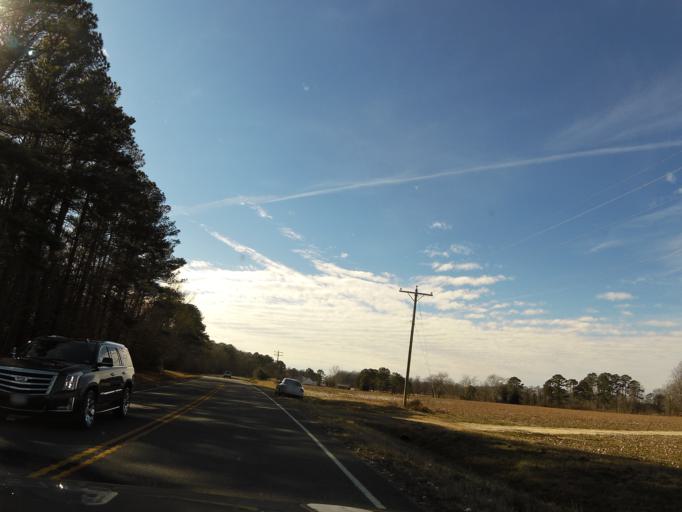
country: US
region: Virginia
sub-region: Isle of Wight County
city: Windsor
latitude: 36.7840
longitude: -76.8166
